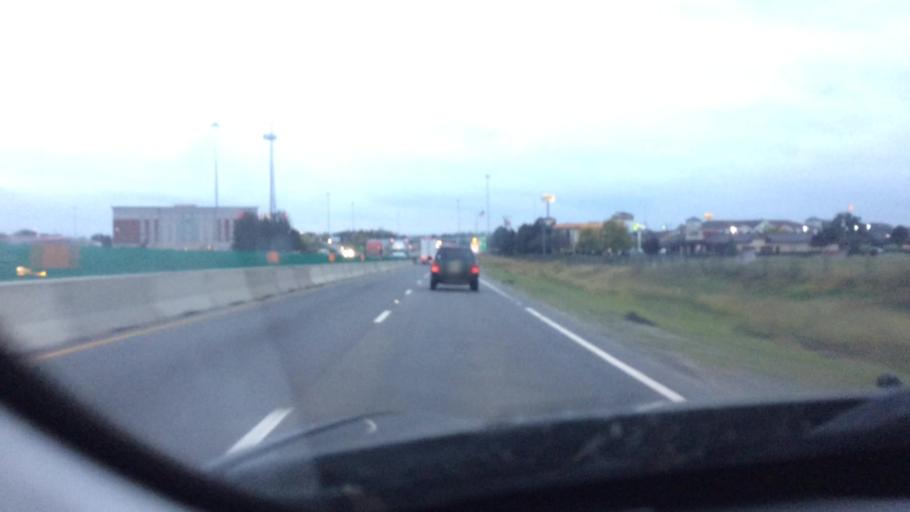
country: US
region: Ohio
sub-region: Hancock County
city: Findlay
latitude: 41.0638
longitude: -83.6662
